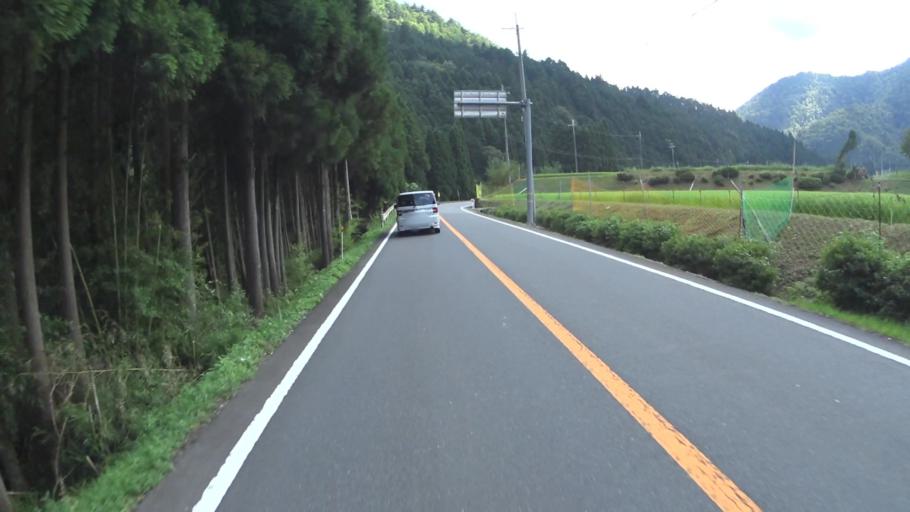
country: JP
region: Kyoto
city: Maizuru
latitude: 35.2923
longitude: 135.5572
